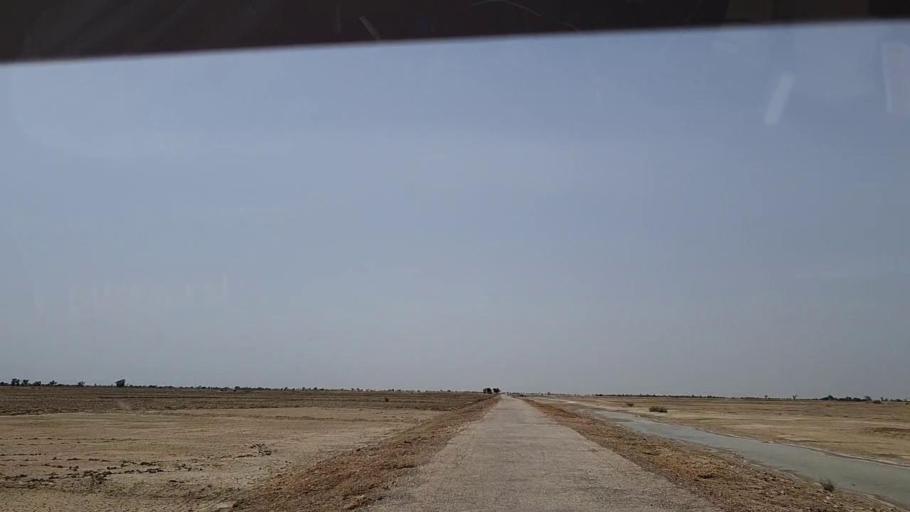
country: PK
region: Sindh
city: Johi
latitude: 26.7264
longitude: 67.6412
